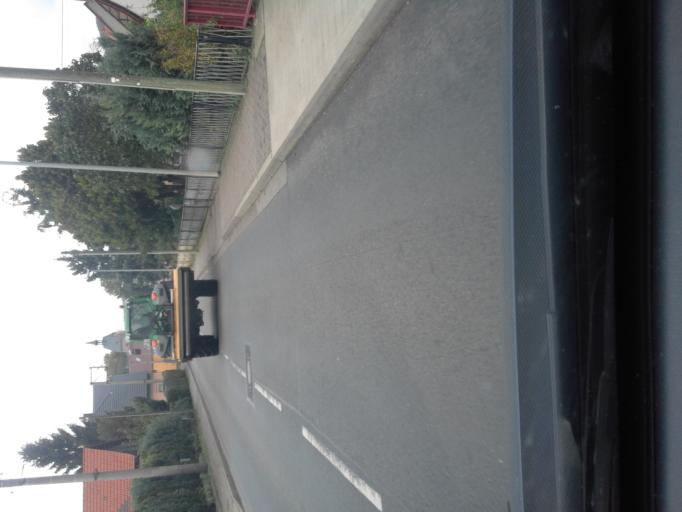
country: DE
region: Thuringia
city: Ostramondra
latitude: 51.1962
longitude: 11.3594
